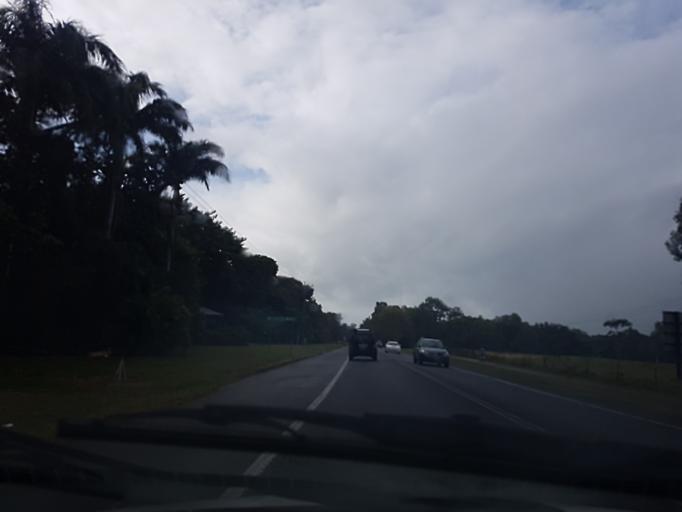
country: AU
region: Queensland
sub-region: Cairns
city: Trinity Beach
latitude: -16.7809
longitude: 145.6737
